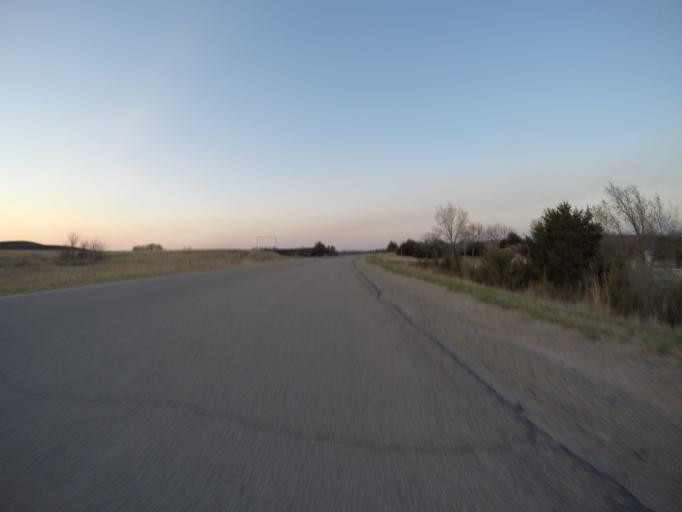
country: US
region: Kansas
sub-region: Riley County
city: Ogden
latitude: 39.0687
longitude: -96.6571
